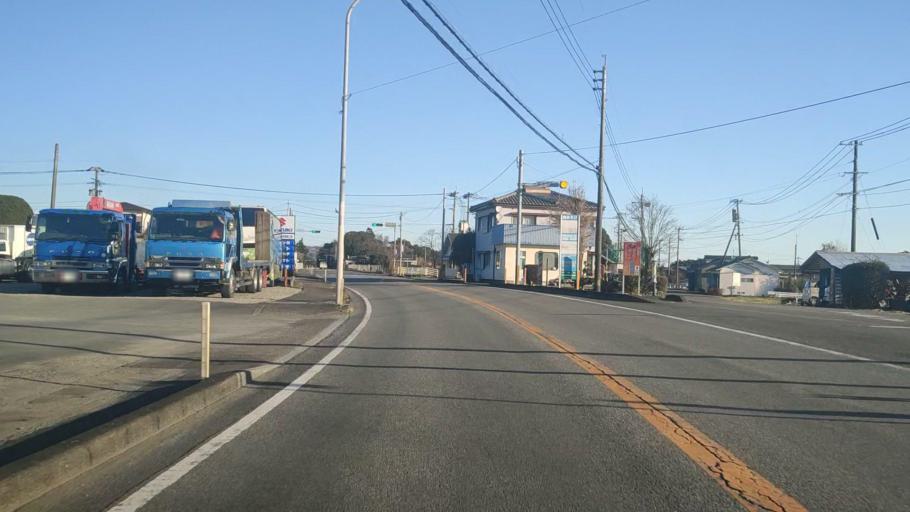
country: JP
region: Miyazaki
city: Takanabe
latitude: 32.2312
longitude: 131.5483
